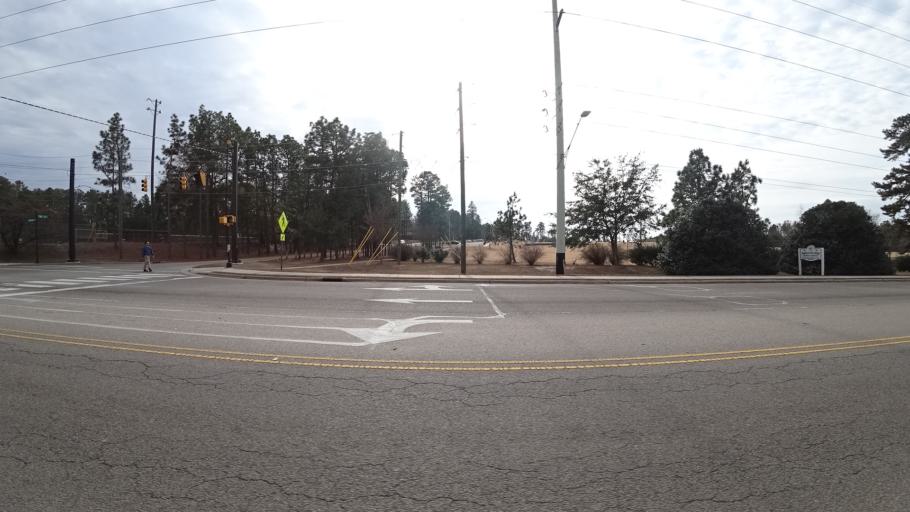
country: US
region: North Carolina
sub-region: Moore County
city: Southern Pines
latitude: 35.1725
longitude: -79.4109
